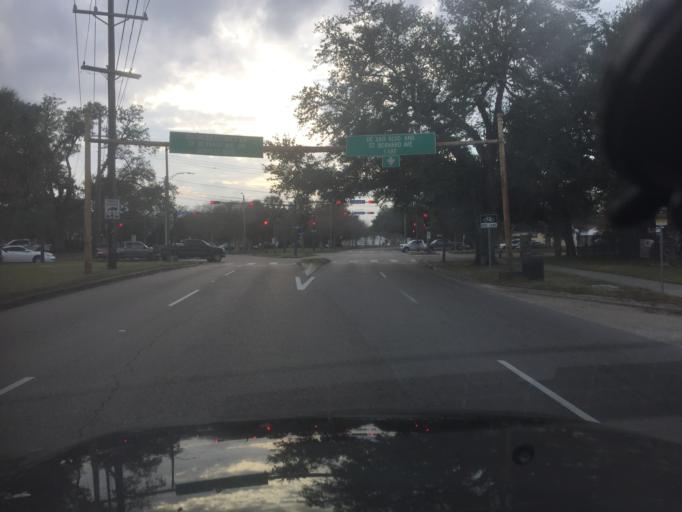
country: US
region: Louisiana
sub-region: Orleans Parish
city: New Orleans
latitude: 29.9889
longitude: -90.0741
